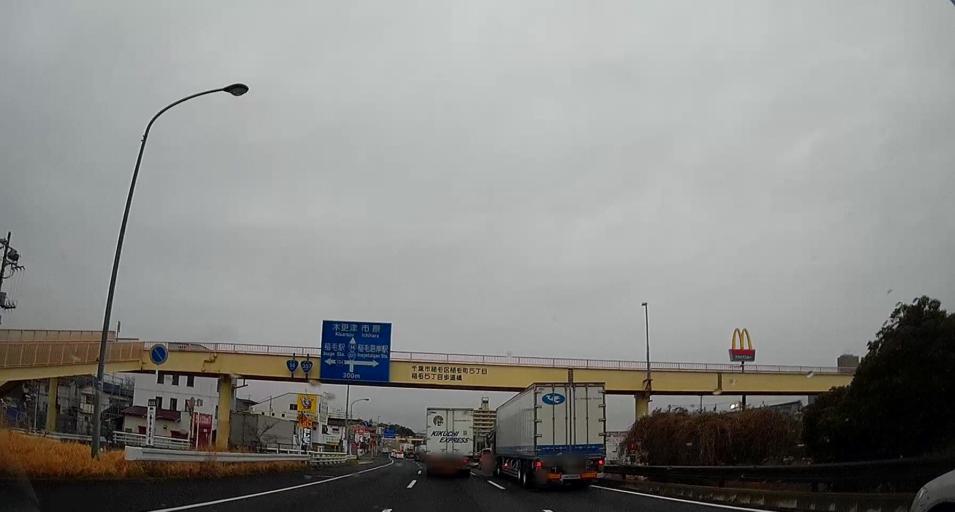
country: JP
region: Chiba
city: Chiba
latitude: 35.6383
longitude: 140.0775
